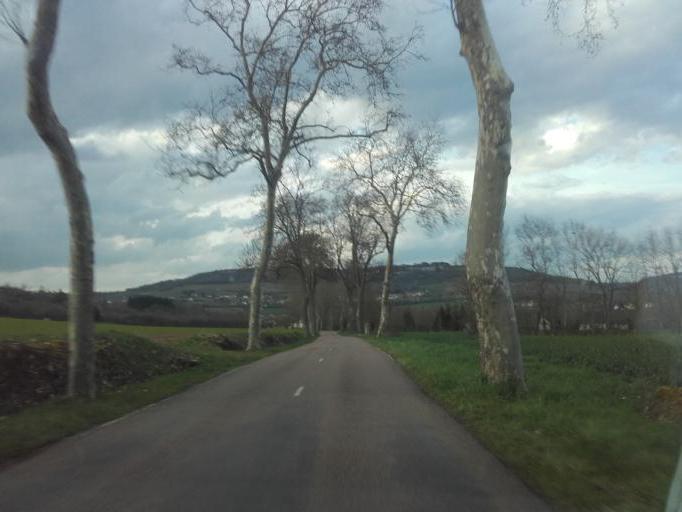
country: FR
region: Bourgogne
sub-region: Departement de la Cote-d'Or
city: Nolay
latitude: 46.9426
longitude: 4.6225
